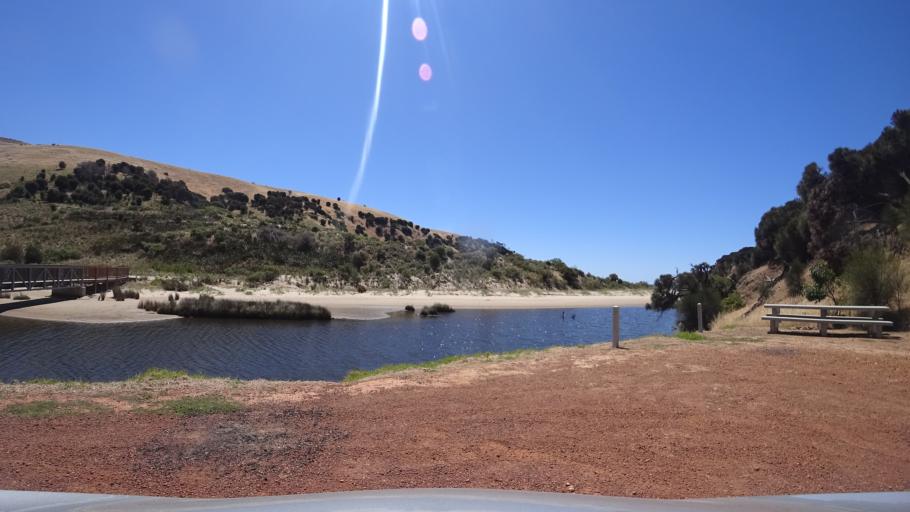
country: AU
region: South Australia
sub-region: Kangaroo Island
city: Kingscote
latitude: -35.6773
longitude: 136.9715
